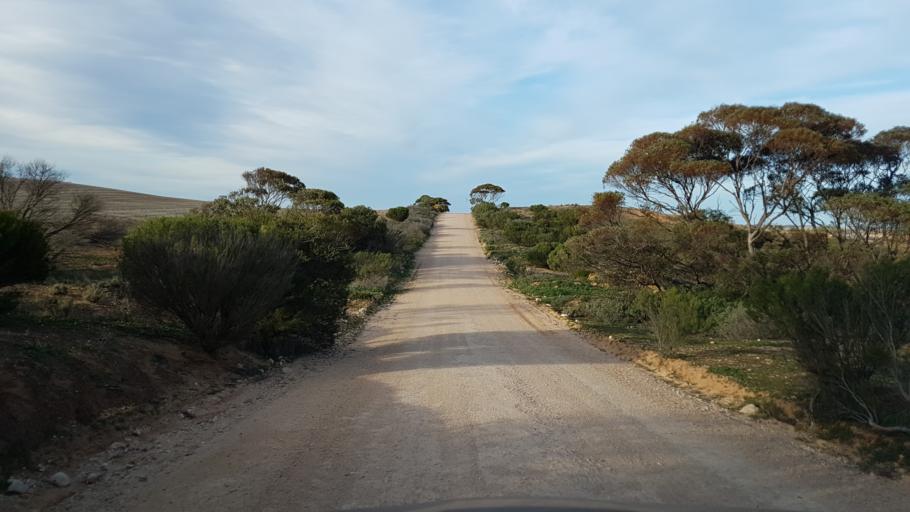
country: AU
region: South Australia
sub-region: Mid Murray
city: Mannum
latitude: -34.7516
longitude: 139.5740
